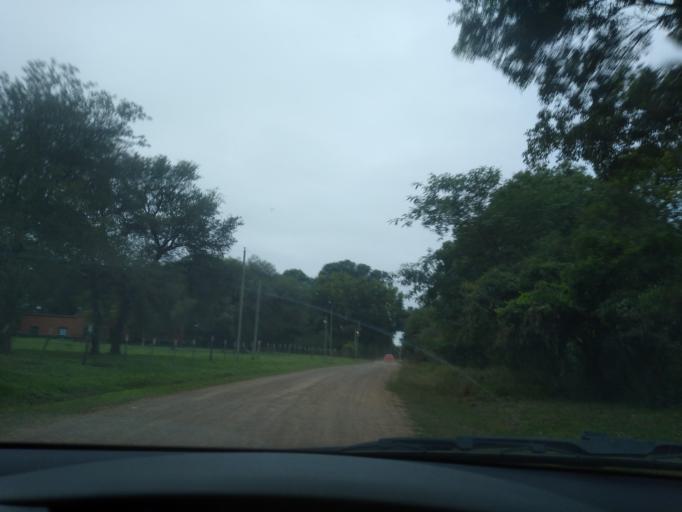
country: AR
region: Chaco
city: Colonia Benitez
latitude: -27.3343
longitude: -58.9650
